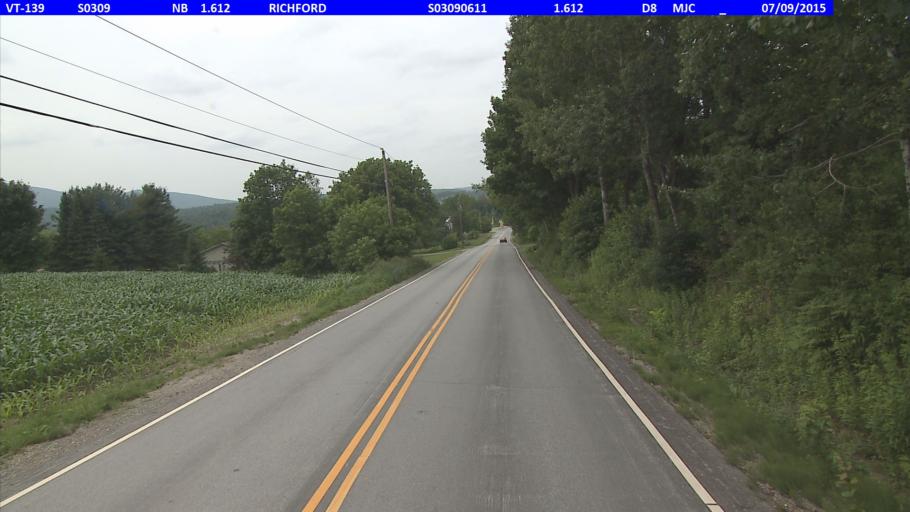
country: US
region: Vermont
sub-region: Franklin County
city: Richford
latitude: 45.0111
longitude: -72.6615
